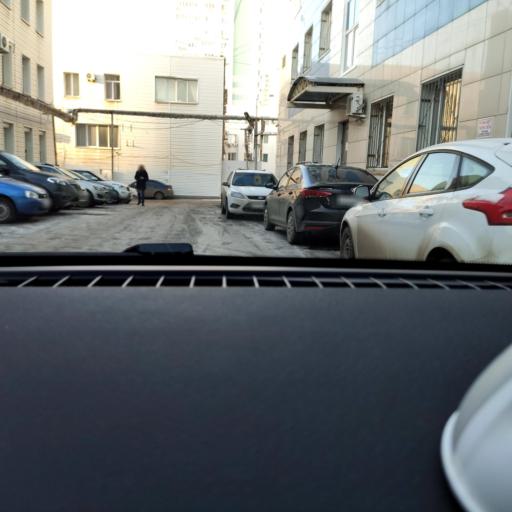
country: RU
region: Samara
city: Samara
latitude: 53.2198
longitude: 50.1952
